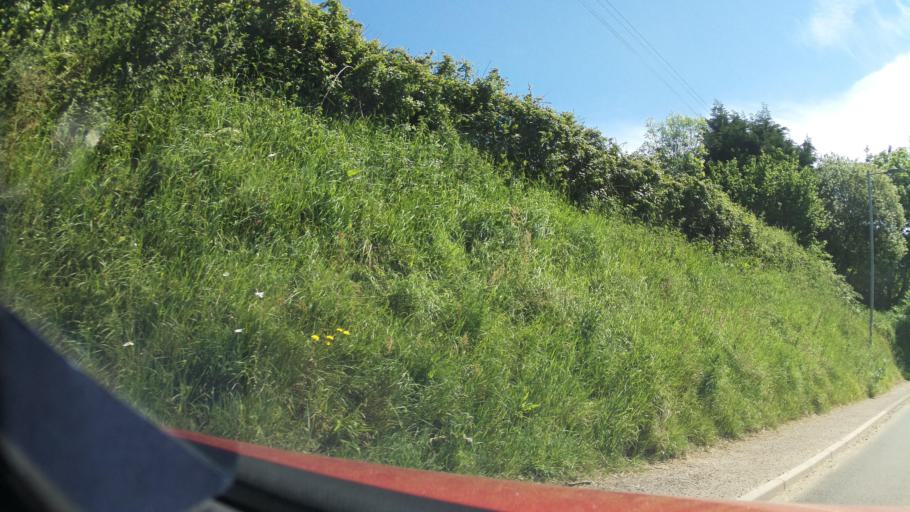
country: GB
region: England
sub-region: Devon
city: Honiton
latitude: 50.8098
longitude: -3.2327
